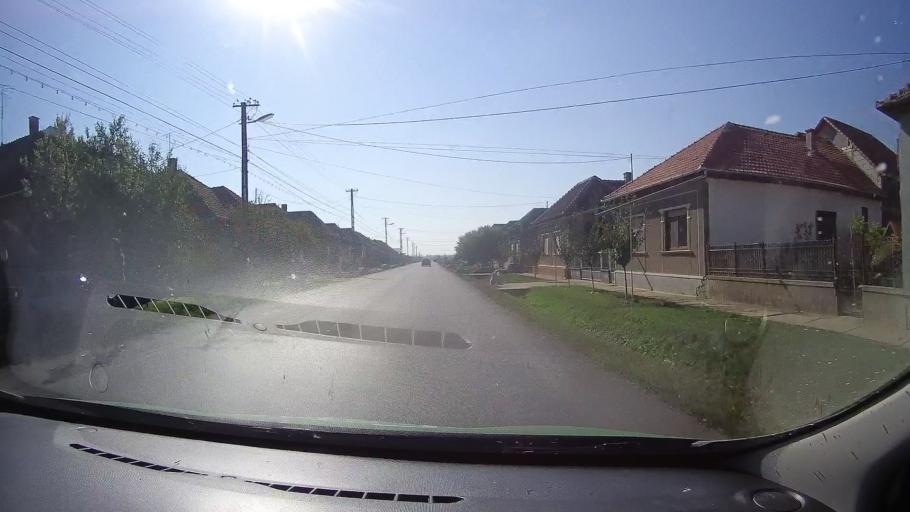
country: RO
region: Satu Mare
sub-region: Comuna Camin
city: Camin
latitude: 47.7248
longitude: 22.4761
